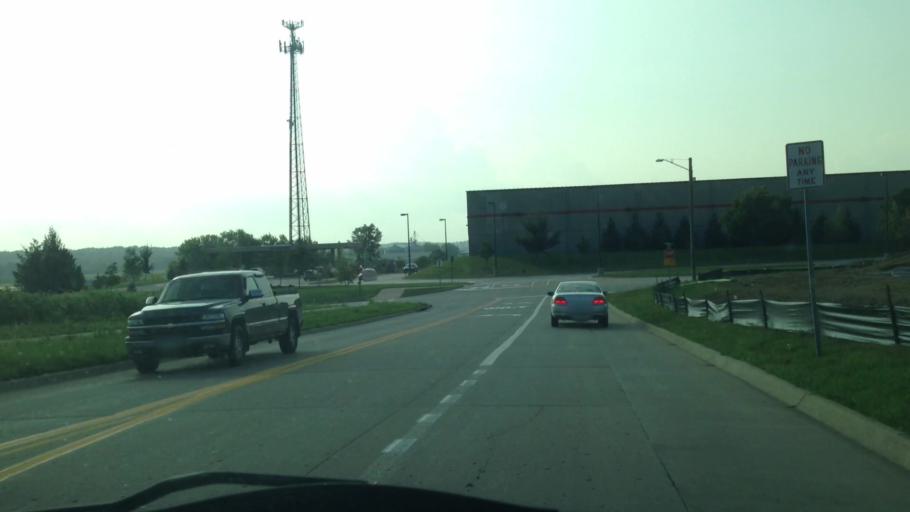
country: US
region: Iowa
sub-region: Johnson County
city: Coralville
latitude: 41.6957
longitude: -91.6164
